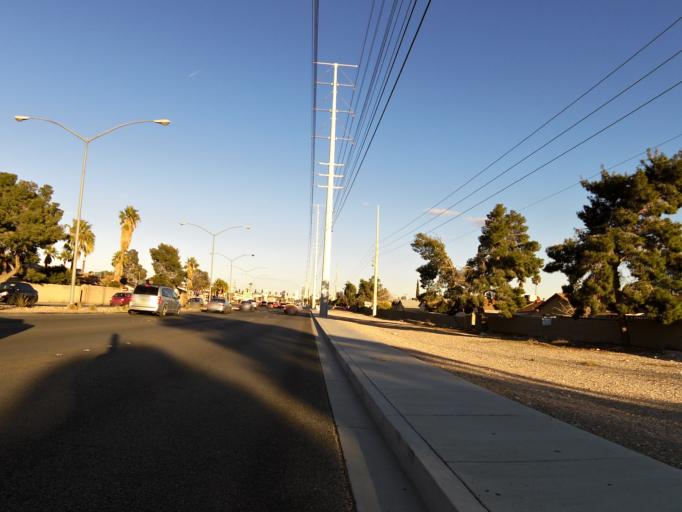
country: US
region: Nevada
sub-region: Clark County
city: Spring Valley
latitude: 36.1144
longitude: -115.2455
